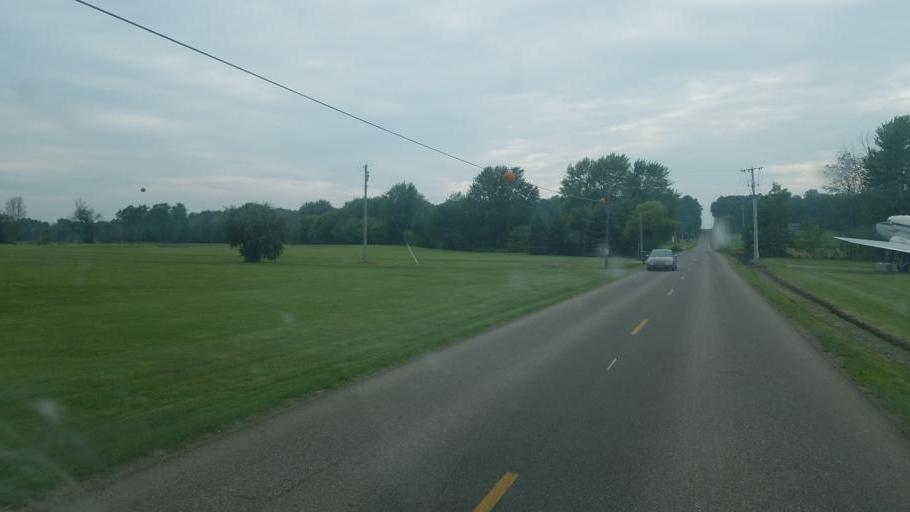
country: US
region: Ohio
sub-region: Wayne County
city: Apple Creek
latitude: 40.7559
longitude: -81.7792
